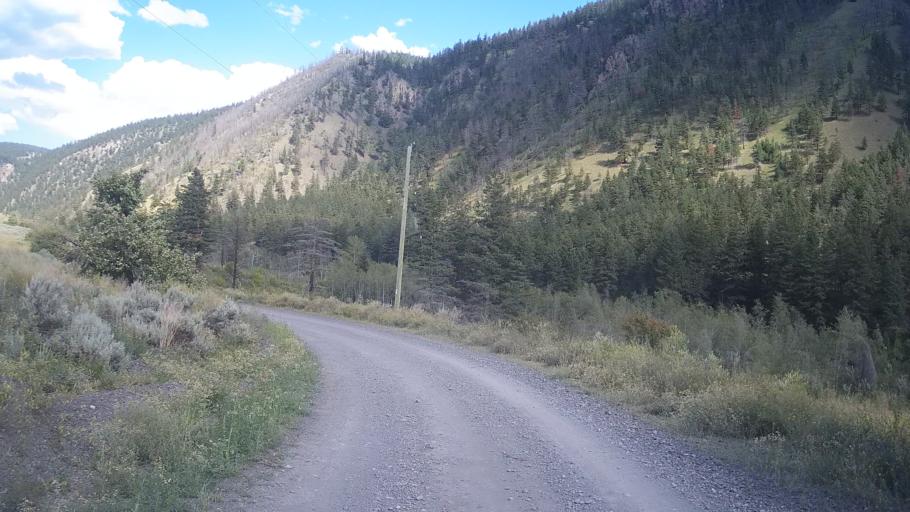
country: CA
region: British Columbia
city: Lillooet
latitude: 51.2199
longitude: -122.0803
